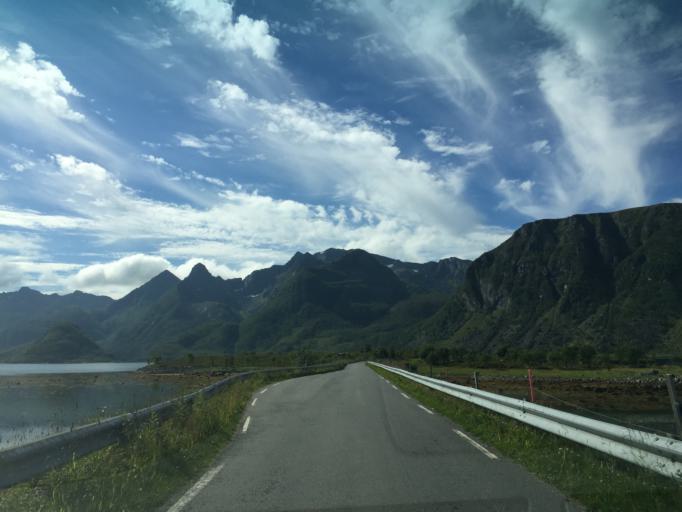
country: NO
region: Nordland
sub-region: Vagan
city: Svolvaer
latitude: 68.3963
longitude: 14.5637
